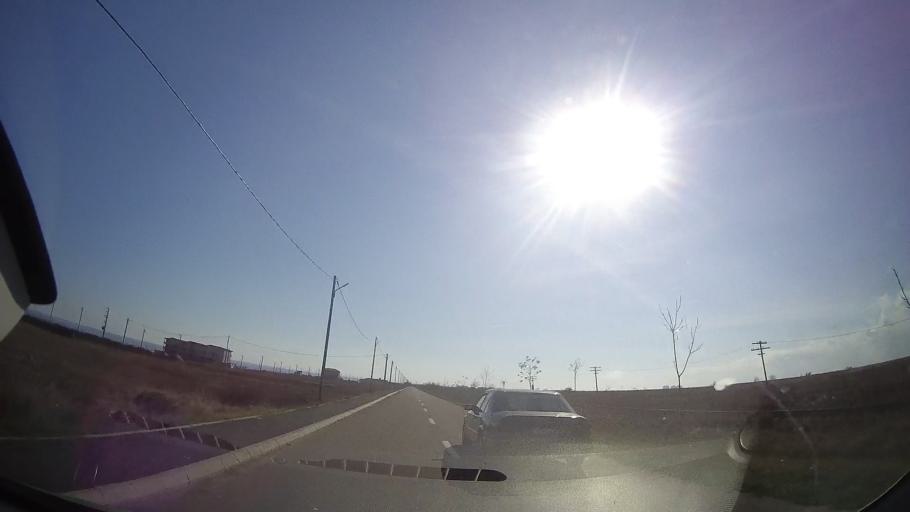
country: RO
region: Constanta
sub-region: Comuna Costinesti
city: Schitu
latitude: 43.9330
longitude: 28.6311
